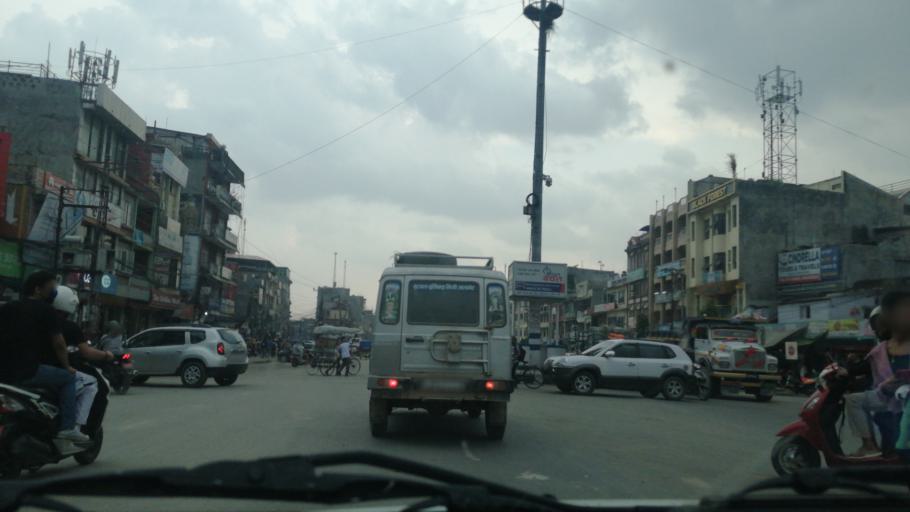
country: NP
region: Western Region
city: Butwal
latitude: 27.7022
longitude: 83.4664
